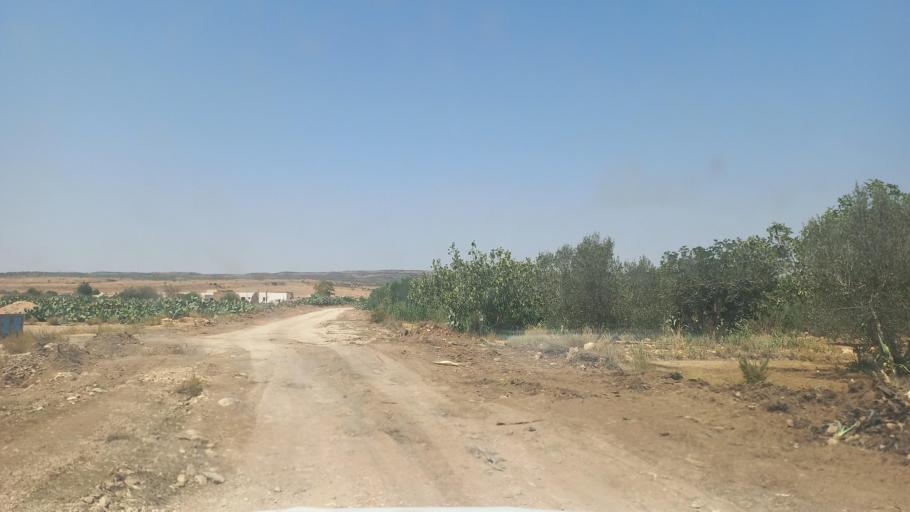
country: TN
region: Al Qasrayn
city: Kasserine
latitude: 35.2934
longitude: 8.9482
